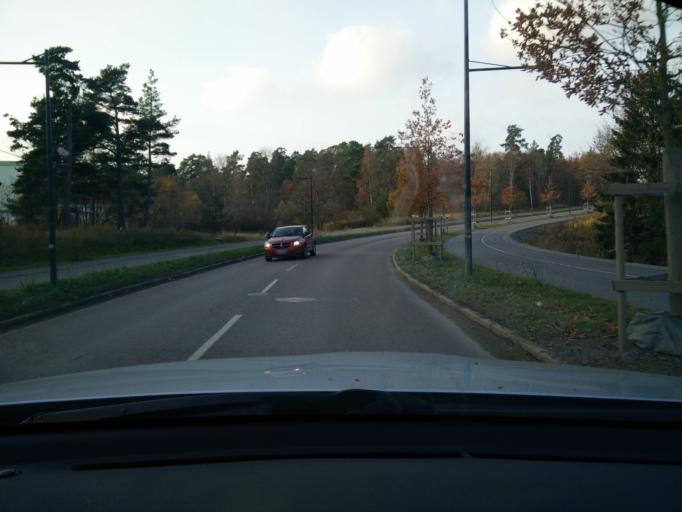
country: SE
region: Stockholm
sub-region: Taby Kommun
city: Taby
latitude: 59.4714
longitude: 18.1306
